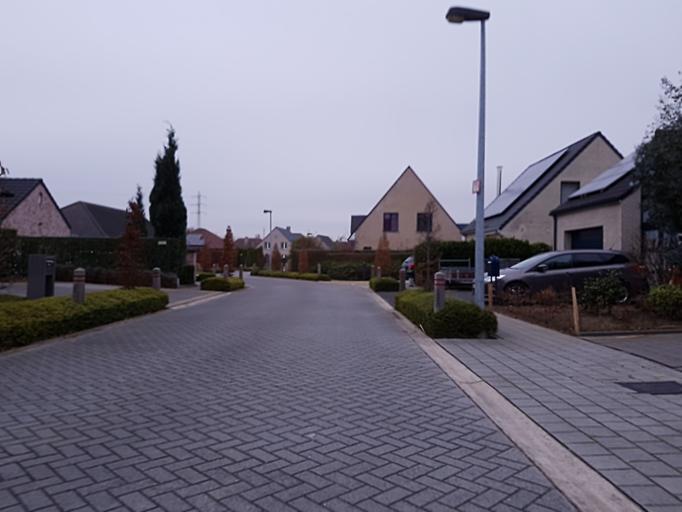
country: BE
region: Flanders
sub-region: Provincie Antwerpen
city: Rumst
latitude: 51.0329
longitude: 4.4145
